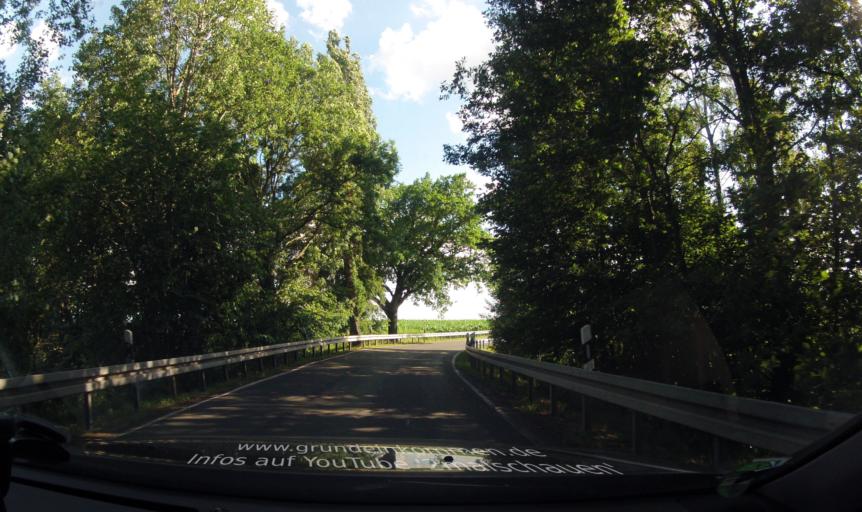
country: DE
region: Saxony
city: Falkenhain
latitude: 51.4080
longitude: 12.8845
